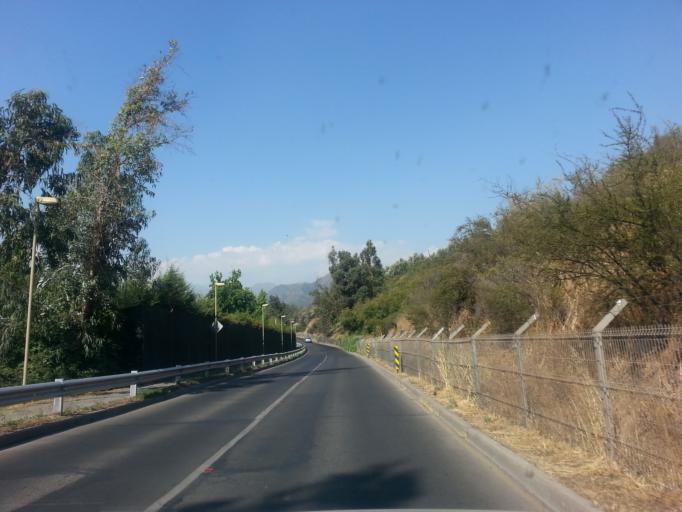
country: CL
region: Santiago Metropolitan
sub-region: Provincia de Santiago
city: Villa Presidente Frei, Nunoa, Santiago, Chile
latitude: -33.3834
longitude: -70.5160
